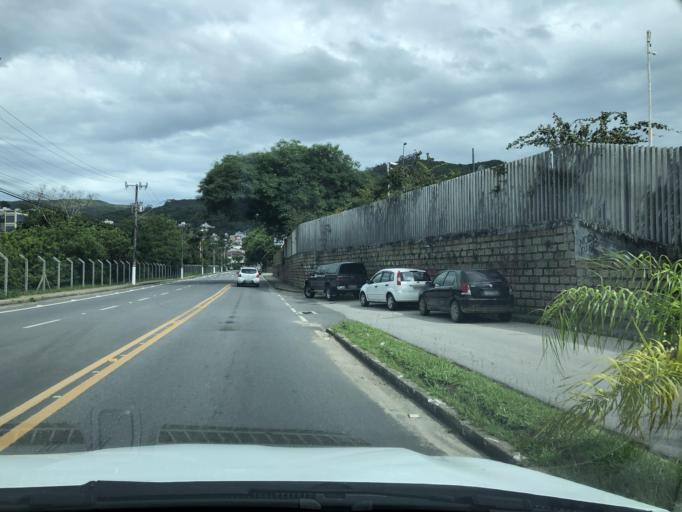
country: BR
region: Santa Catarina
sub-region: Florianopolis
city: Carvoeira
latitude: -27.6046
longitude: -48.5218
